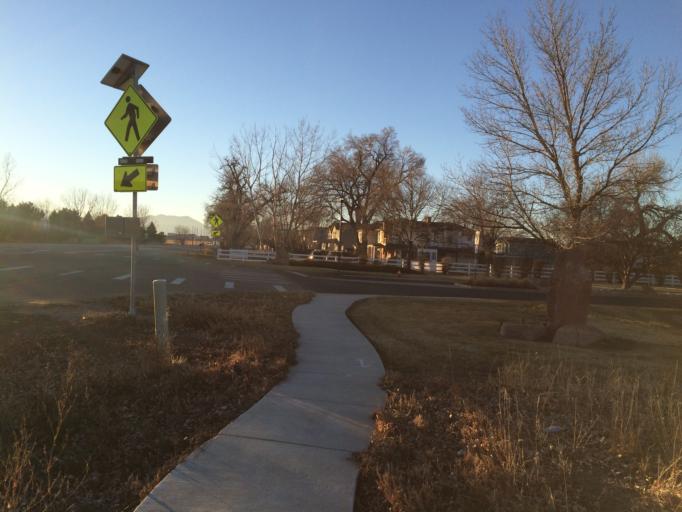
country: US
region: Colorado
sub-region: Boulder County
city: Lafayette
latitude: 39.9725
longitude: -105.0947
